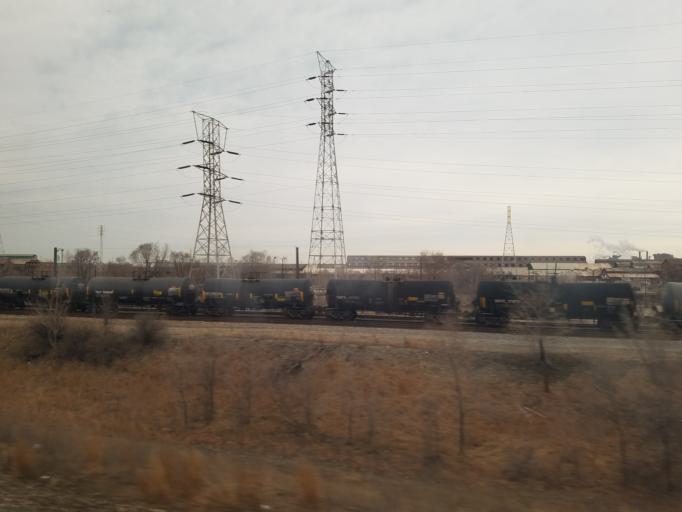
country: US
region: Indiana
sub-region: Lake County
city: Gary
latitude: 41.6101
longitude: -87.3465
